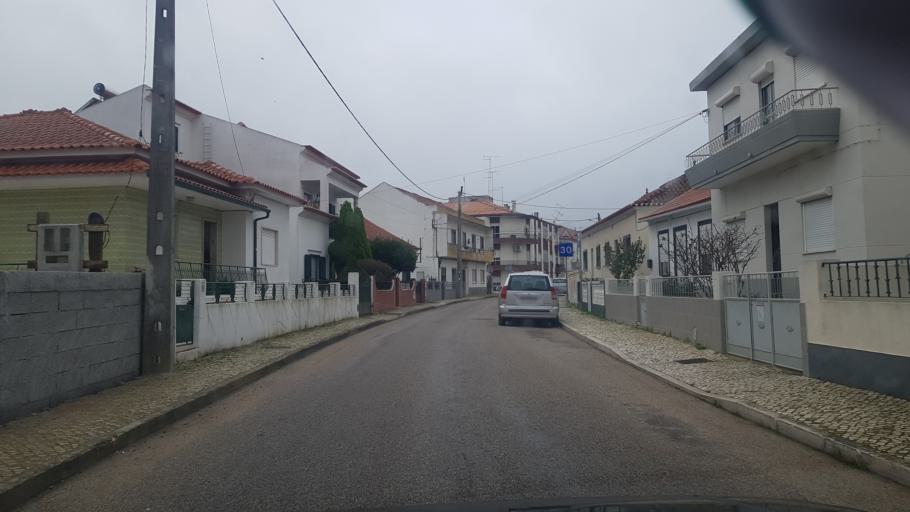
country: PT
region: Santarem
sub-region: Entroncamento
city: Entroncamento
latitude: 39.4662
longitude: -8.4792
